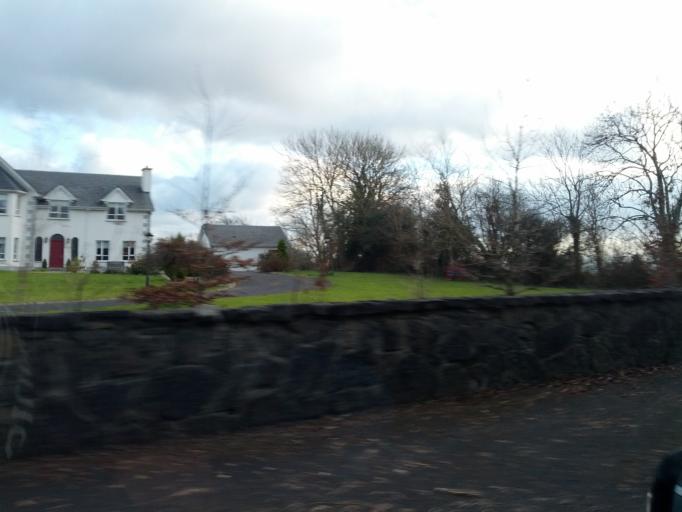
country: IE
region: Connaught
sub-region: County Galway
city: Athenry
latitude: 53.3557
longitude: -8.6548
